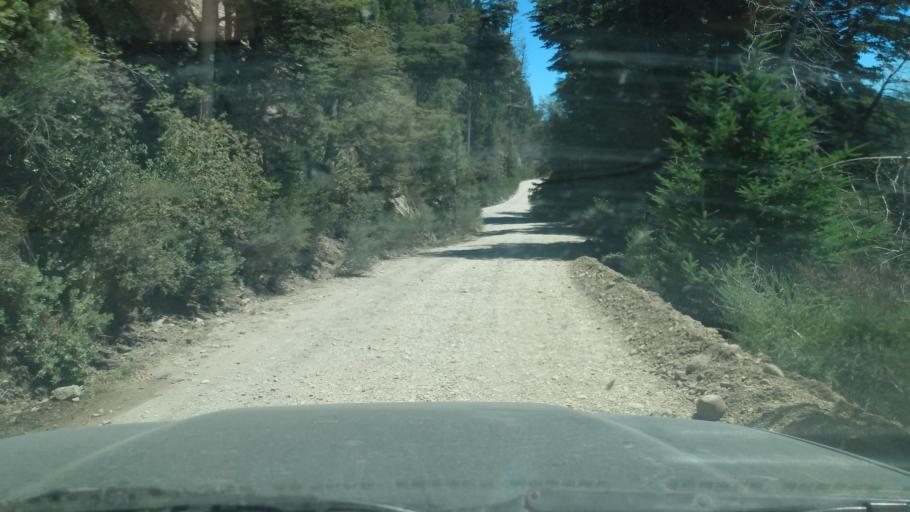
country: AR
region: Rio Negro
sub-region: Departamento de Bariloche
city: San Carlos de Bariloche
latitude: -41.0992
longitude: -71.5043
